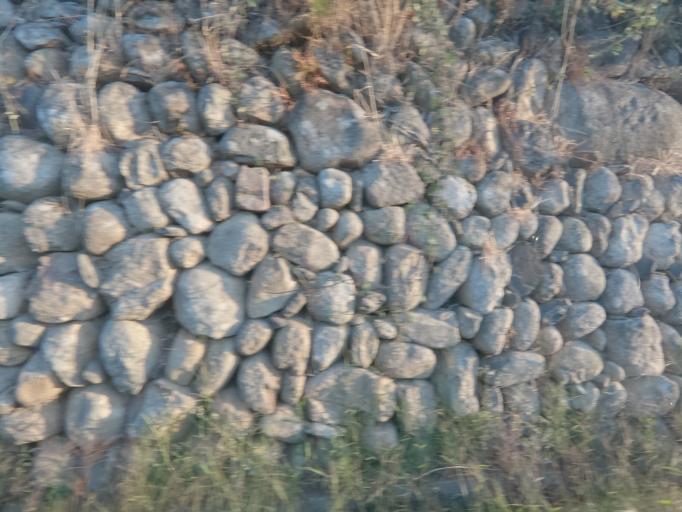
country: PT
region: Vila Real
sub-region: Vila Real
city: Vila Real
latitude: 41.3164
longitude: -7.7648
